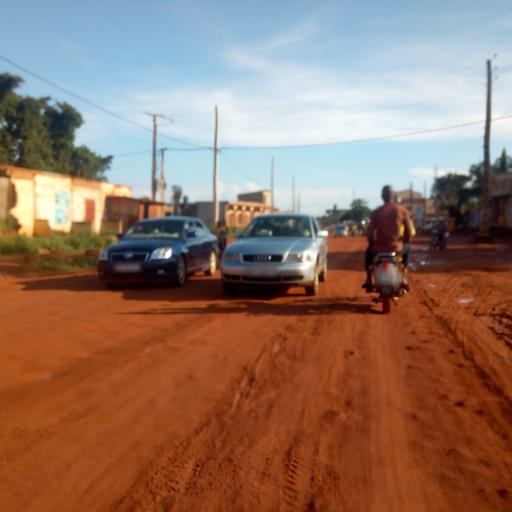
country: BJ
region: Atlantique
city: Hevie
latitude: 6.4087
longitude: 2.2656
